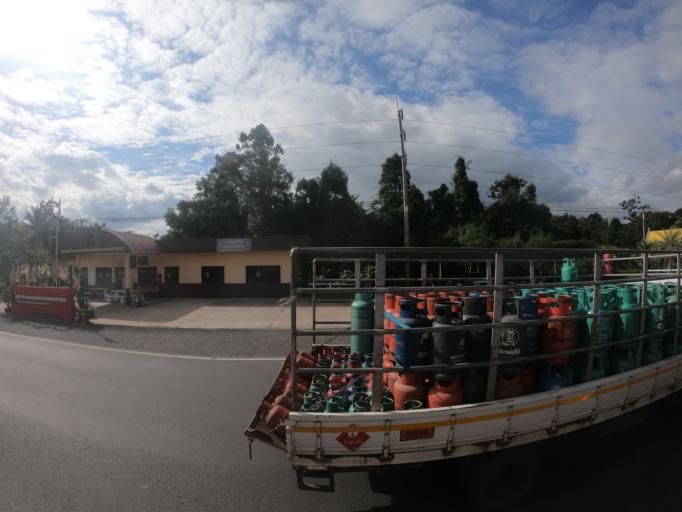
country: TH
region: Surin
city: Prasat
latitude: 14.6276
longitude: 103.3937
